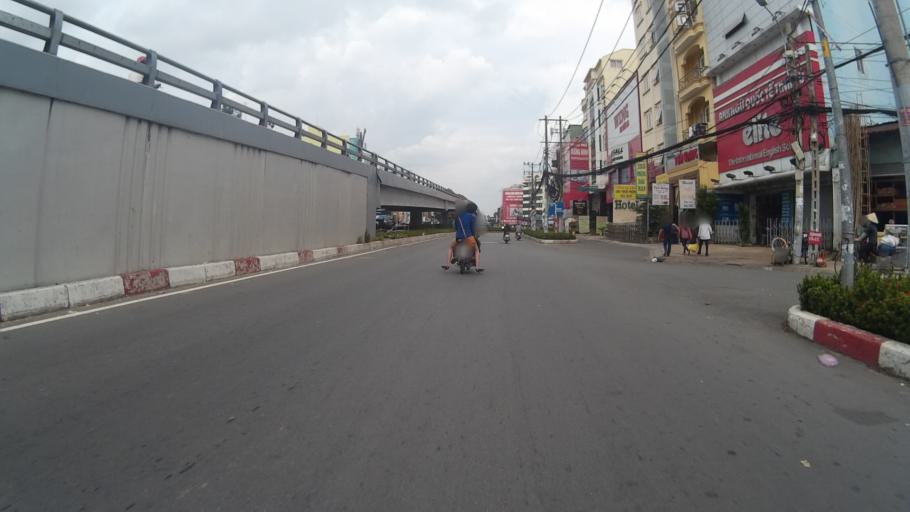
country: VN
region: Ho Chi Minh City
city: Quan Phu Nhuan
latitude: 10.8007
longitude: 106.6600
